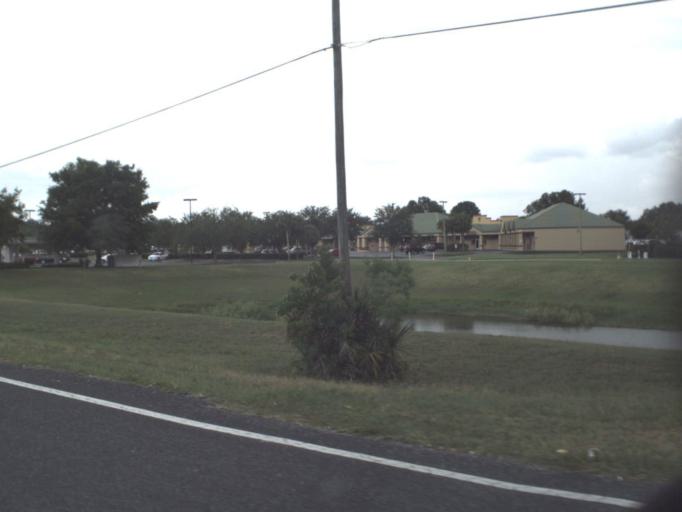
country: US
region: Florida
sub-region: Sumter County
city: The Villages
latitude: 28.9647
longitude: -81.9702
